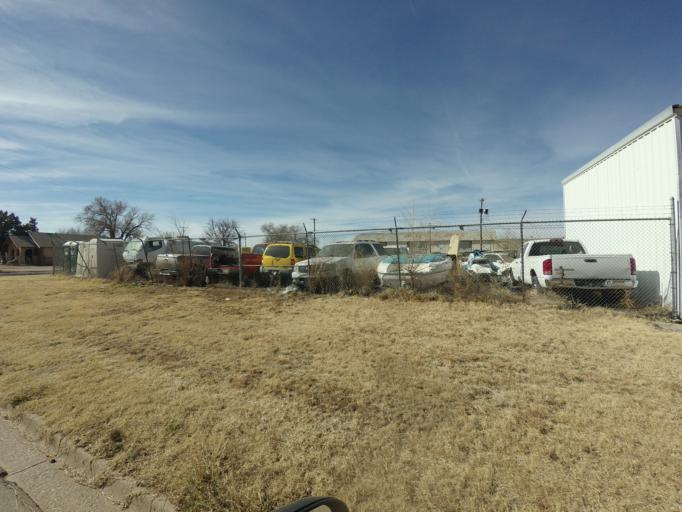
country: US
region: New Mexico
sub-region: Curry County
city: Clovis
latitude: 34.4042
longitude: -103.2218
